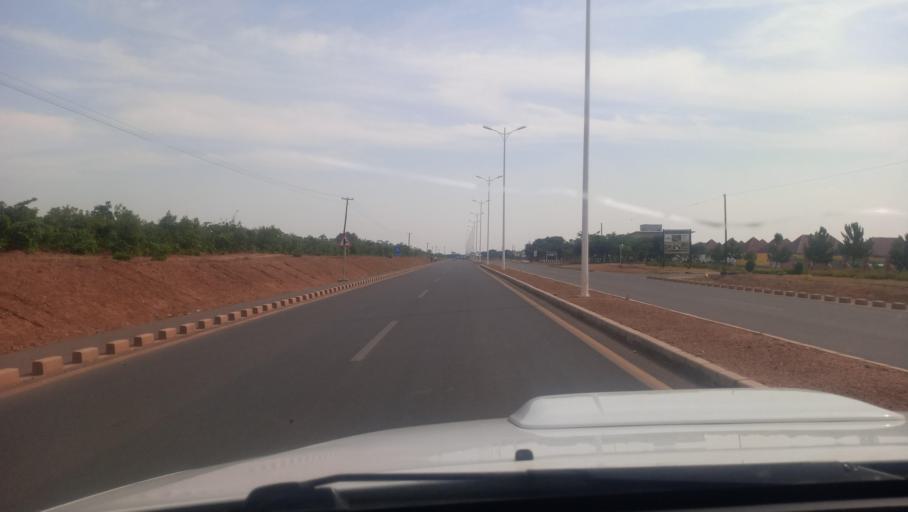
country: ZM
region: Northern
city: Mpika
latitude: -11.8487
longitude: 31.4422
